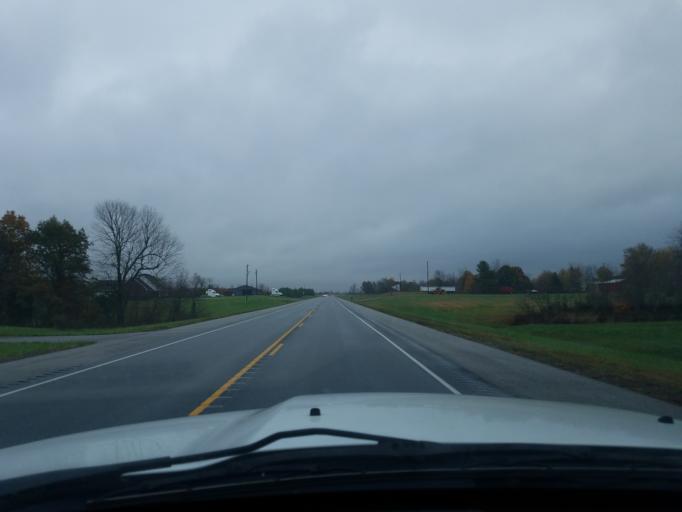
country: US
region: Kentucky
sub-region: Larue County
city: Hodgenville
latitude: 37.5196
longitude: -85.6467
